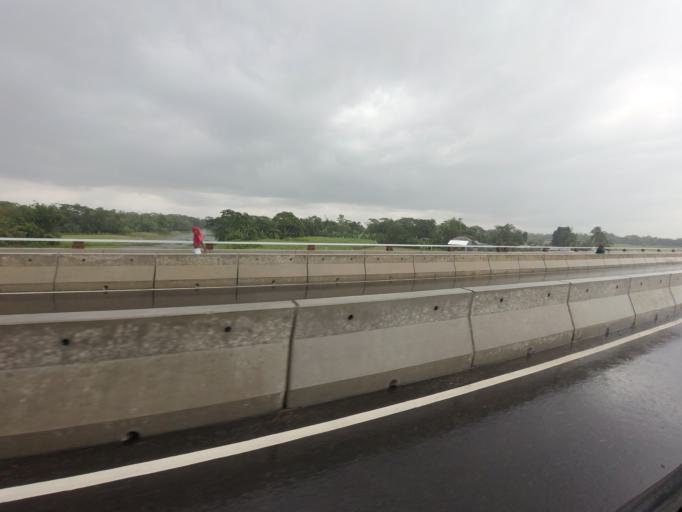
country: BD
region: Dhaka
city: Char Bhadrasan
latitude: 23.4001
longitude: 90.2089
